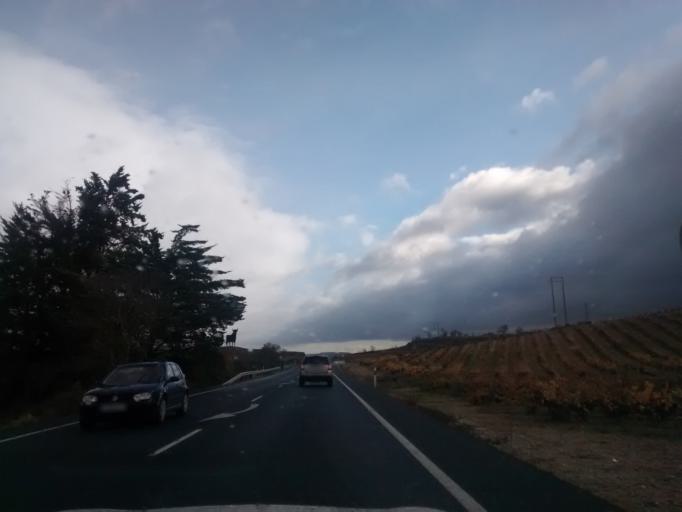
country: ES
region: La Rioja
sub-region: Provincia de La Rioja
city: San Asensio
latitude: 42.5110
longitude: -2.7286
